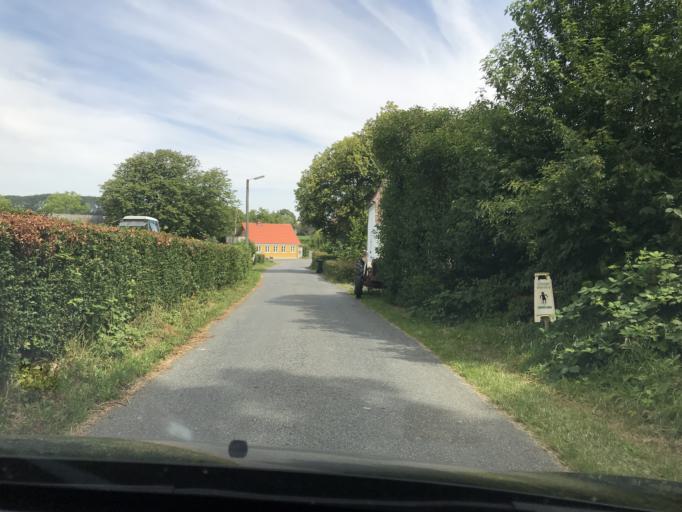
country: DK
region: South Denmark
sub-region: AEro Kommune
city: AEroskobing
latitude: 54.9125
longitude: 10.2811
